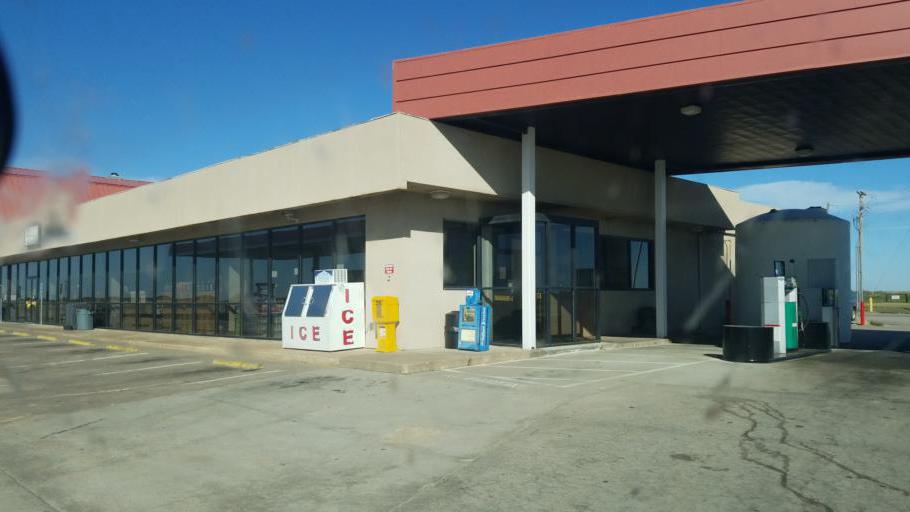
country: US
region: Kansas
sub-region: Russell County
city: Russell
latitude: 38.8583
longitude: -98.7063
